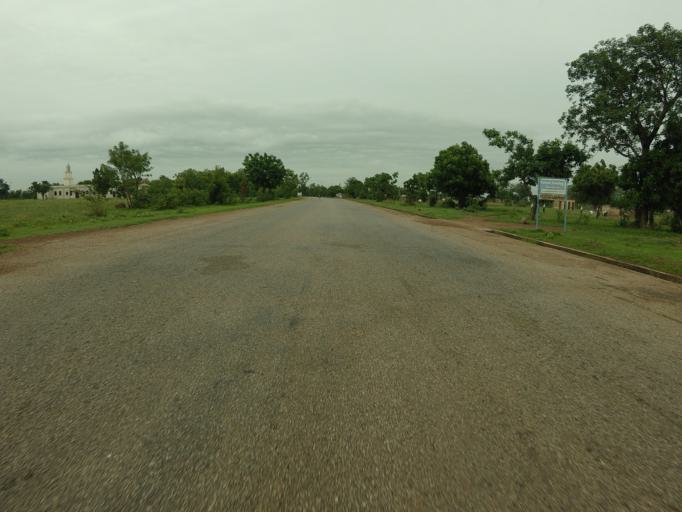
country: GH
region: Northern
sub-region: Yendi
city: Yendi
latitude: 9.5073
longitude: -0.0275
